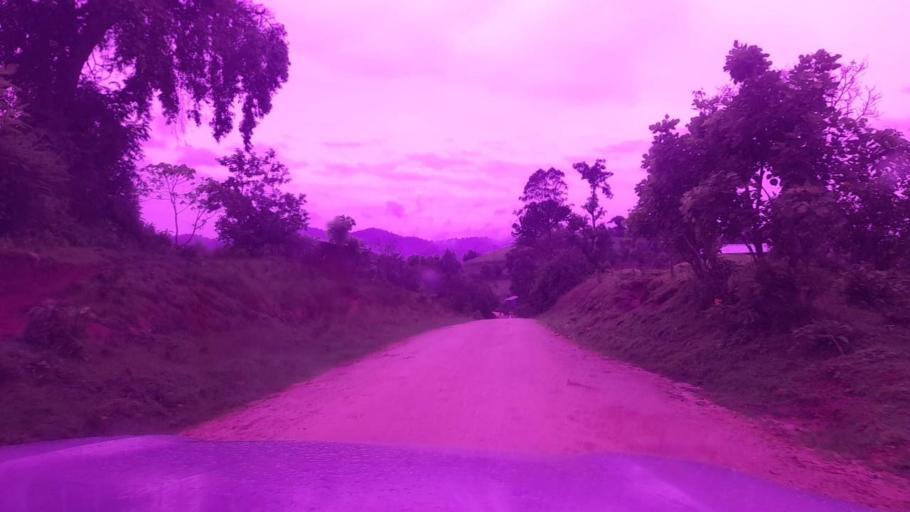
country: ET
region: Southern Nations, Nationalities, and People's Region
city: Bonga
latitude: 7.4535
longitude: 36.1274
